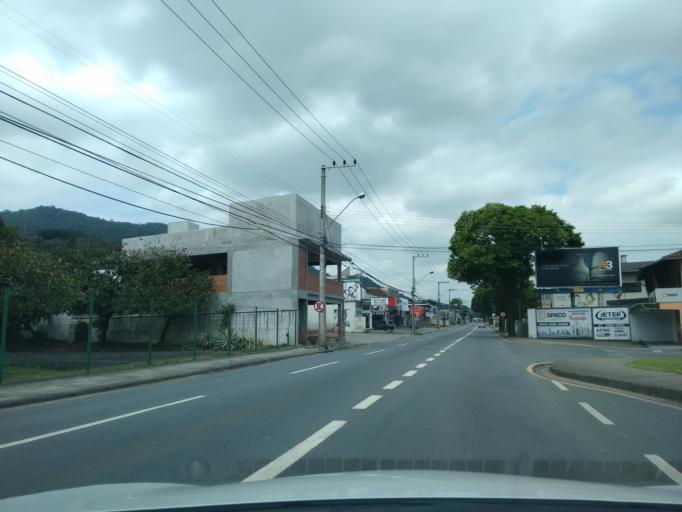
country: BR
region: Santa Catarina
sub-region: Jaragua Do Sul
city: Jaragua do Sul
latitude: -26.4812
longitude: -49.0638
